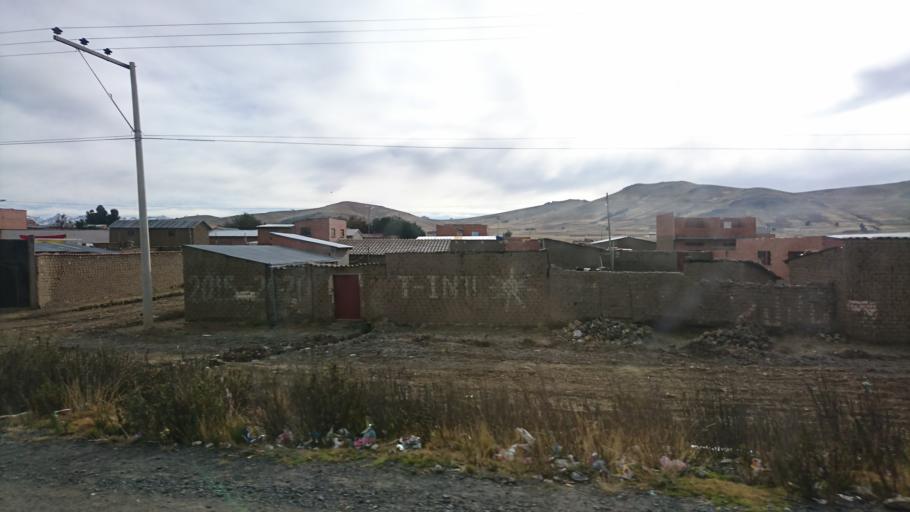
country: BO
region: La Paz
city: Batallas
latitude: -16.3790
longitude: -68.3780
